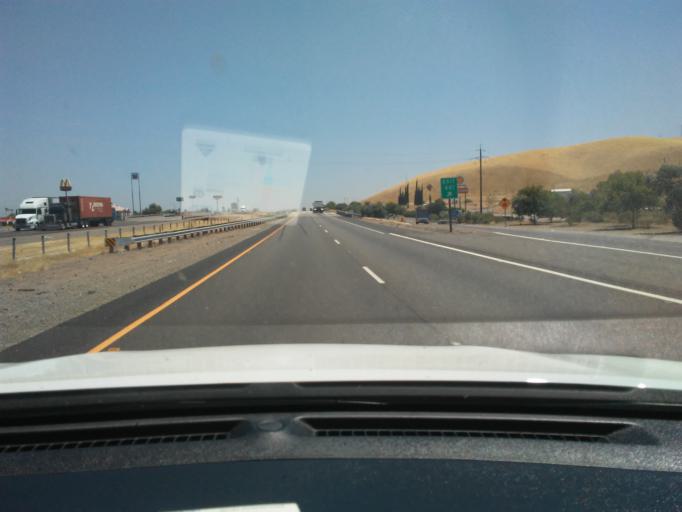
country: US
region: California
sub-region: Stanislaus County
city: Patterson
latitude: 37.5416
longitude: -121.2699
